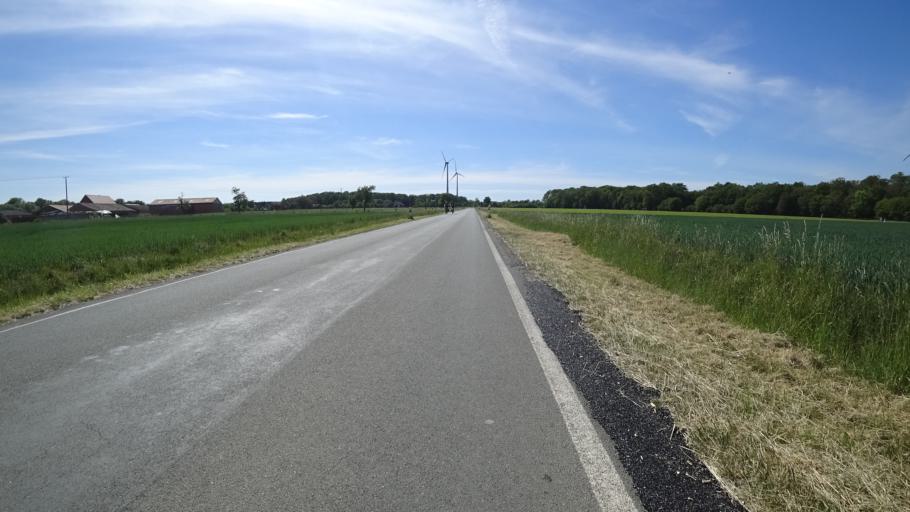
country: DE
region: North Rhine-Westphalia
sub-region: Regierungsbezirk Detmold
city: Rheda-Wiedenbruck
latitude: 51.8246
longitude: 8.2313
